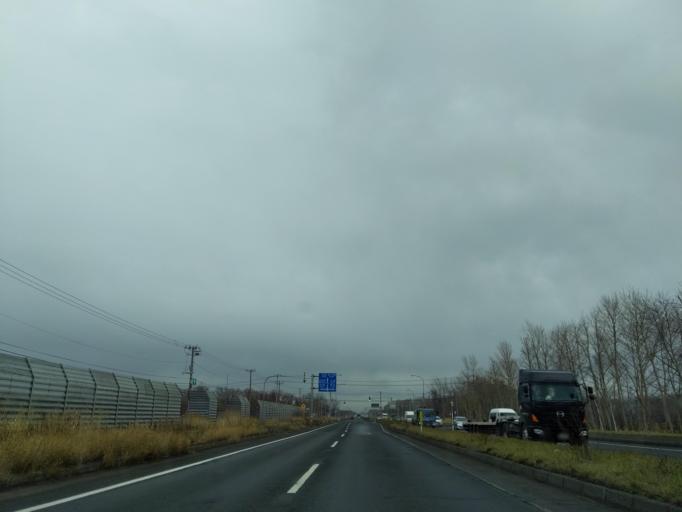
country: JP
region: Hokkaido
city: Ishikari
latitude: 43.1803
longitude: 141.3494
